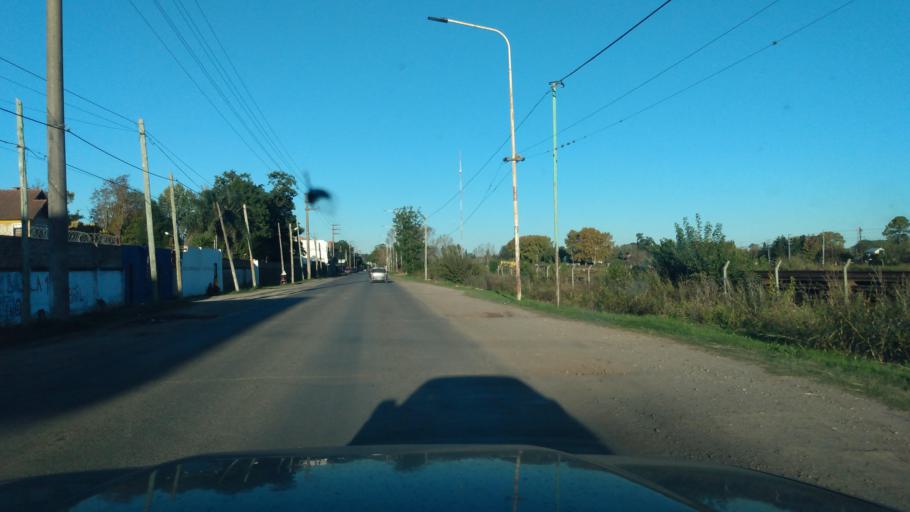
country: AR
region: Buenos Aires
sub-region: Partido de General Rodriguez
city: General Rodriguez
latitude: -34.6300
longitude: -58.8597
